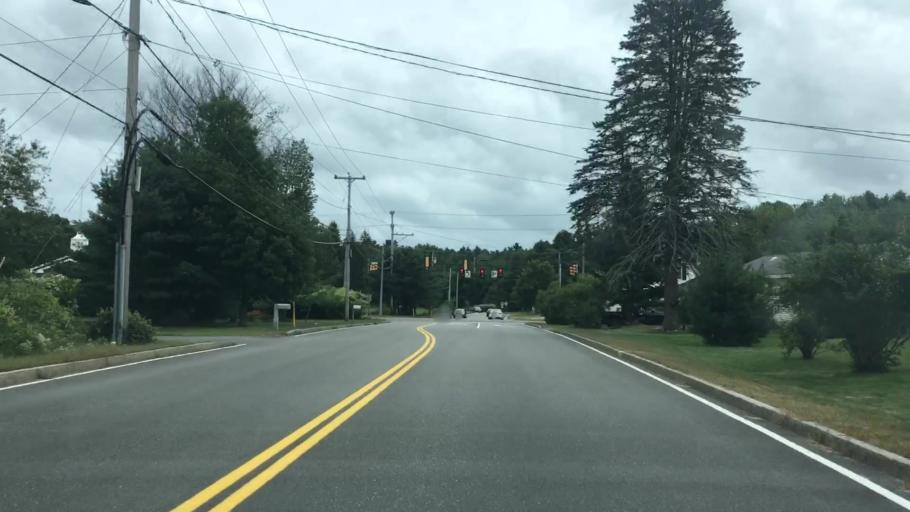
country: US
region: Maine
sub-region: Cumberland County
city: South Portland Gardens
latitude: 43.6199
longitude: -70.3453
